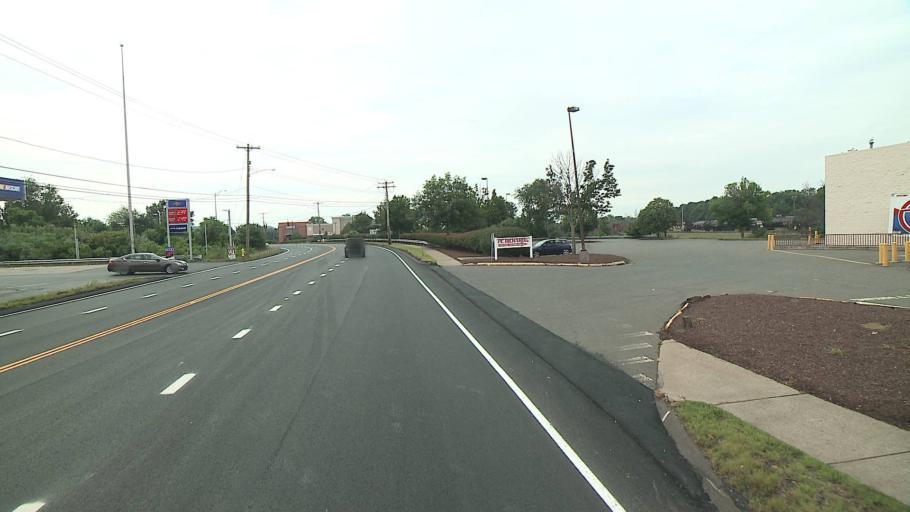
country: US
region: Connecticut
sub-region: New Haven County
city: North Haven
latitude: 41.3501
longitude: -72.8690
